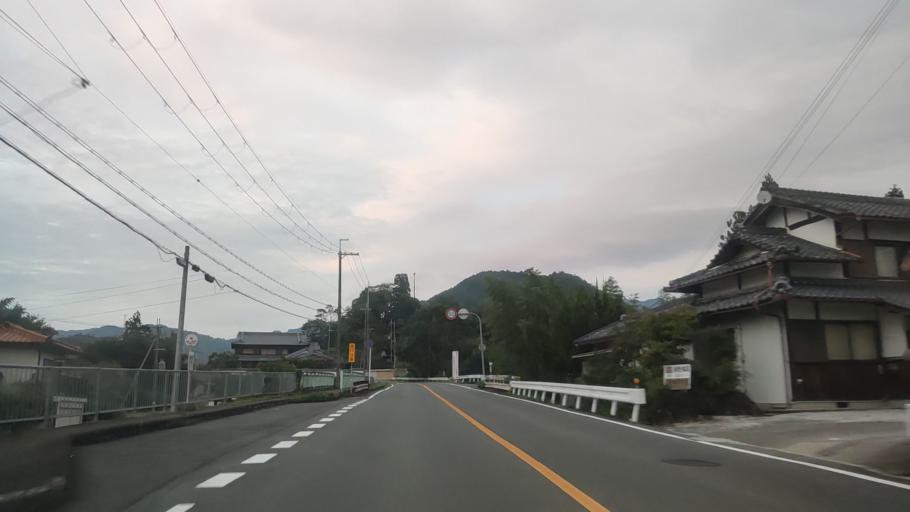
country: JP
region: Wakayama
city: Hashimoto
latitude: 34.3512
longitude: 135.6067
